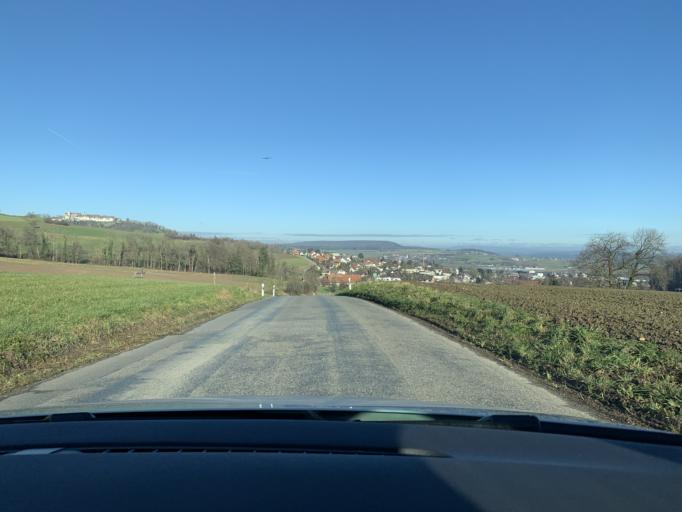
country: CH
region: Zurich
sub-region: Bezirk Dielsdorf
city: Dielsdorf
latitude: 47.4671
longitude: 8.4517
